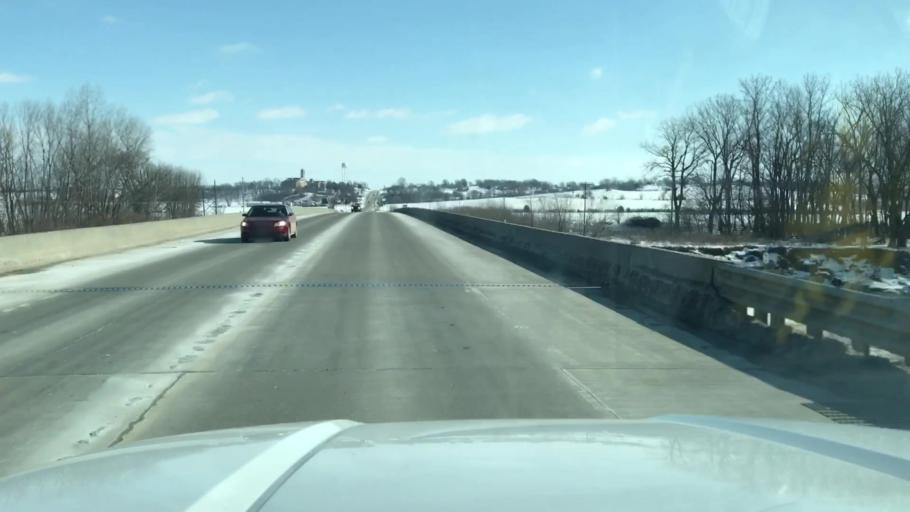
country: US
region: Missouri
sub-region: Nodaway County
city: Maryville
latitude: 40.3449
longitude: -94.8324
